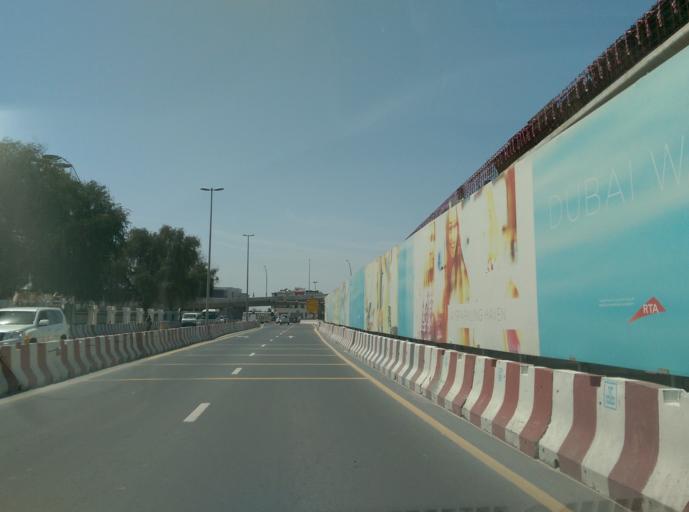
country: AE
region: Dubai
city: Dubai
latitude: 25.1885
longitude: 55.2413
